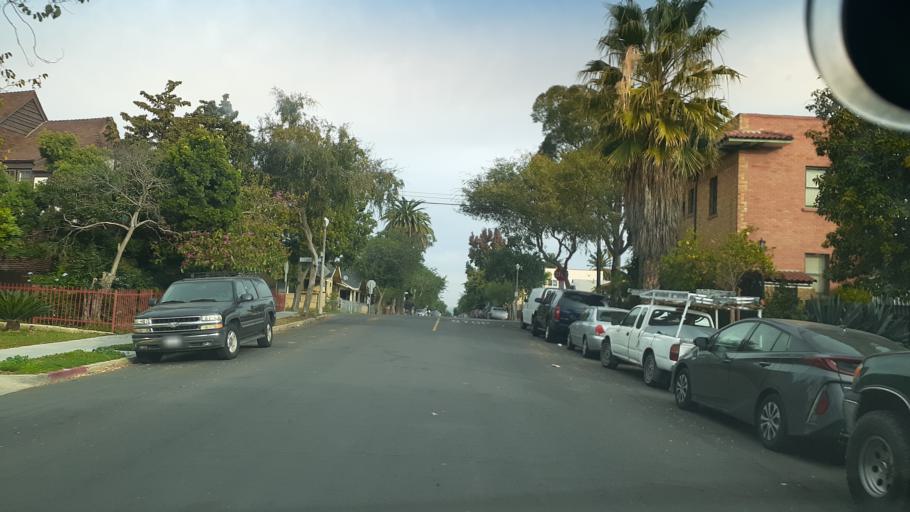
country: US
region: California
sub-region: Los Angeles County
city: Long Beach
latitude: 33.7761
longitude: -118.2006
